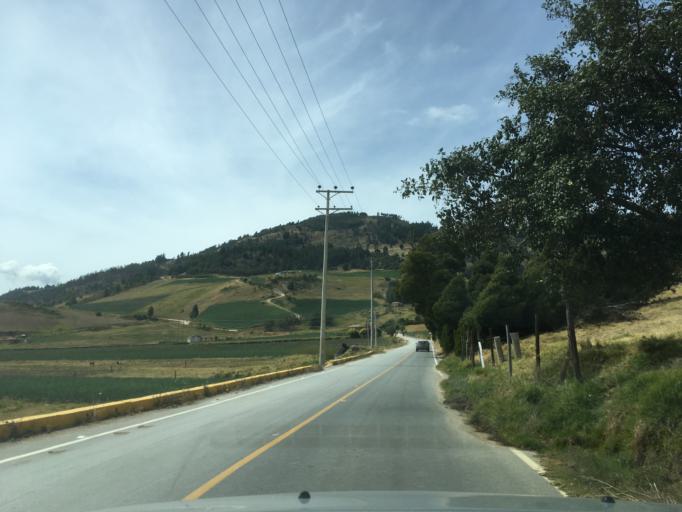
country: CO
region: Boyaca
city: Aquitania
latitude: 5.5979
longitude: -72.9142
